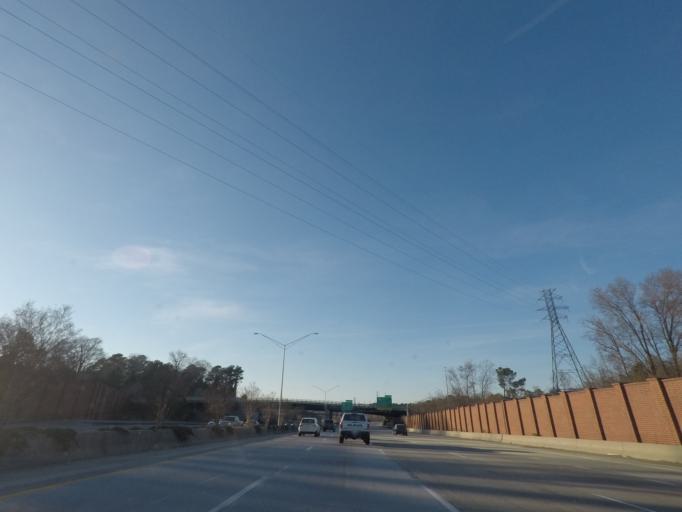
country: US
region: North Carolina
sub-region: Durham County
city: Durham
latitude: 36.0183
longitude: -78.8990
